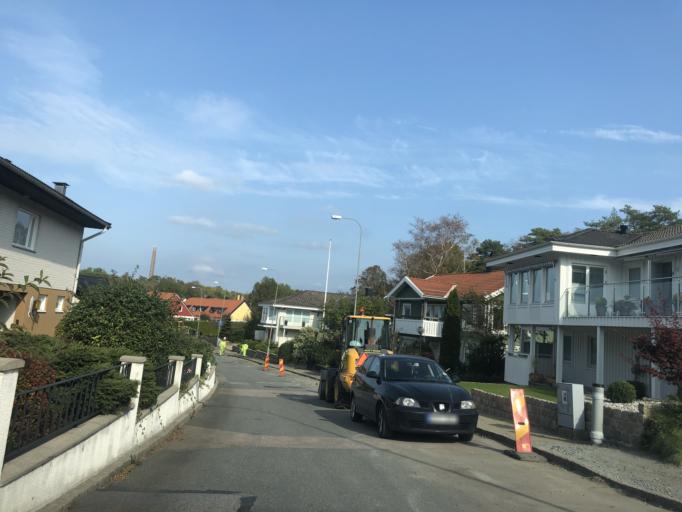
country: SE
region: Vaestra Goetaland
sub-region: Goteborg
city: Majorna
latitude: 57.6444
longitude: 11.8897
